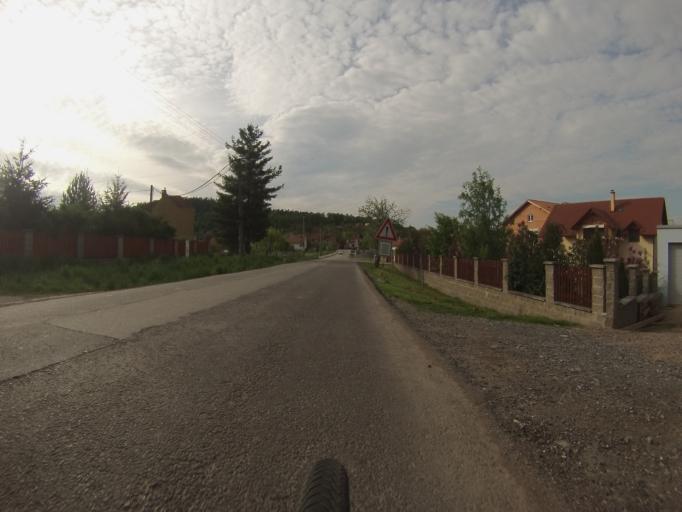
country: CZ
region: South Moravian
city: Cebin
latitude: 49.3125
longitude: 16.4539
